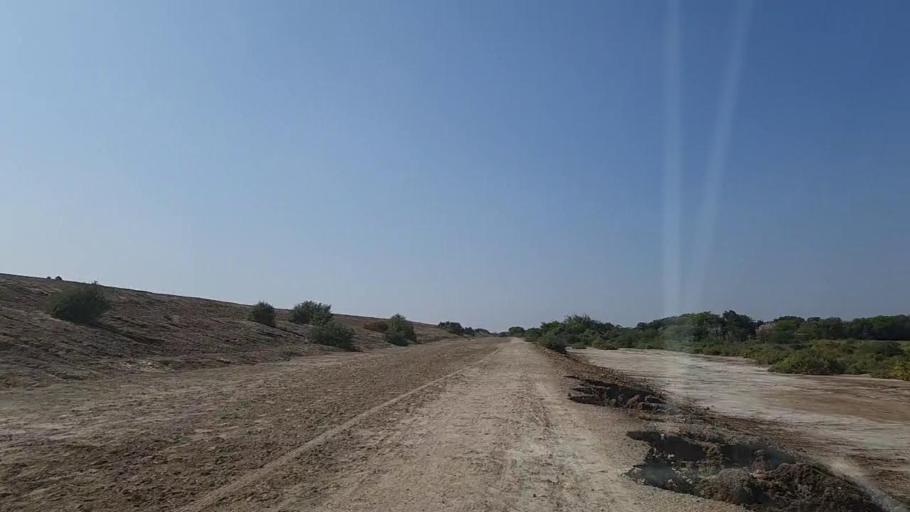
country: PK
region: Sindh
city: Chuhar Jamali
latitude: 24.4888
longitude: 68.0150
